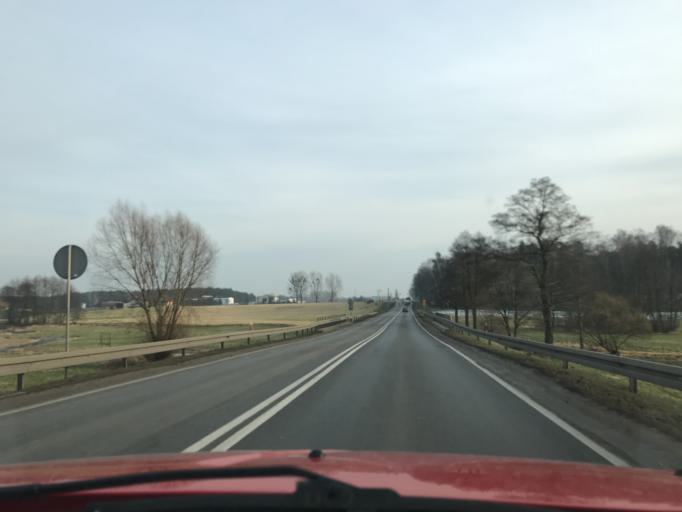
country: PL
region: Greater Poland Voivodeship
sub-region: Powiat jarocinski
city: Kotlin
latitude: 51.9367
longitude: 17.6079
